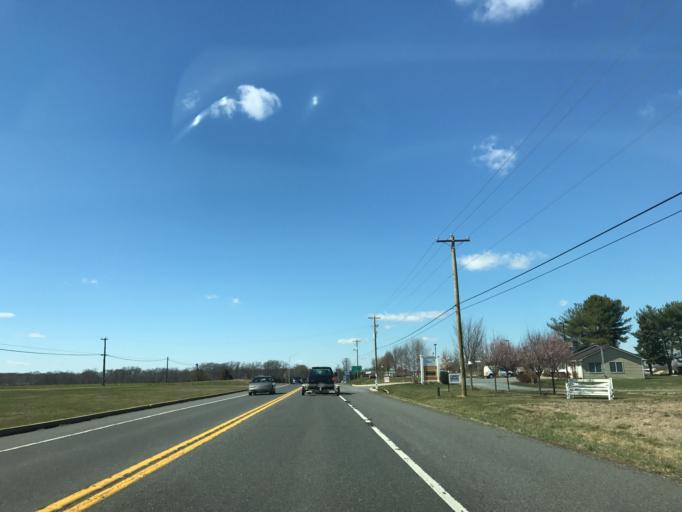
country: US
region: Maryland
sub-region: Queen Anne's County
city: Kingstown
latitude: 39.1949
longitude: -76.0315
